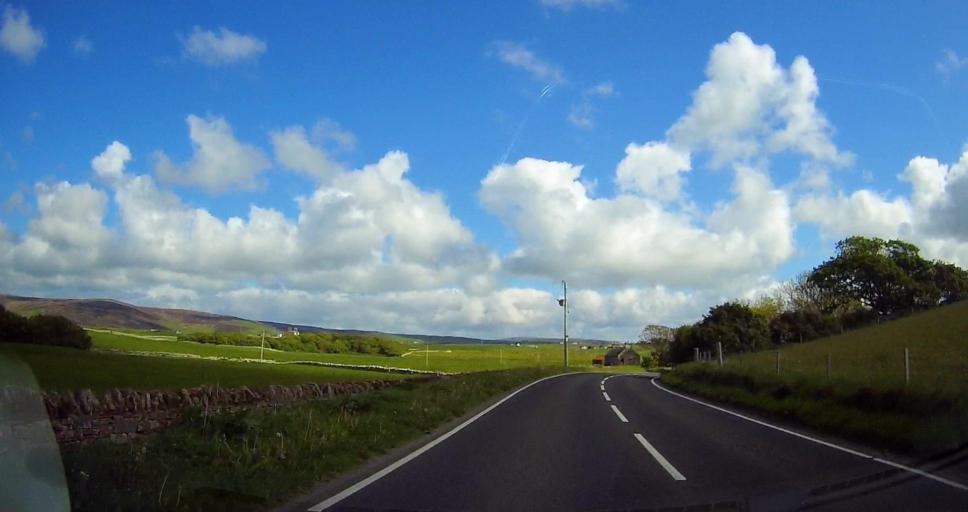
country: GB
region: Scotland
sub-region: Orkney Islands
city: Stromness
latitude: 59.0419
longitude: -3.1883
